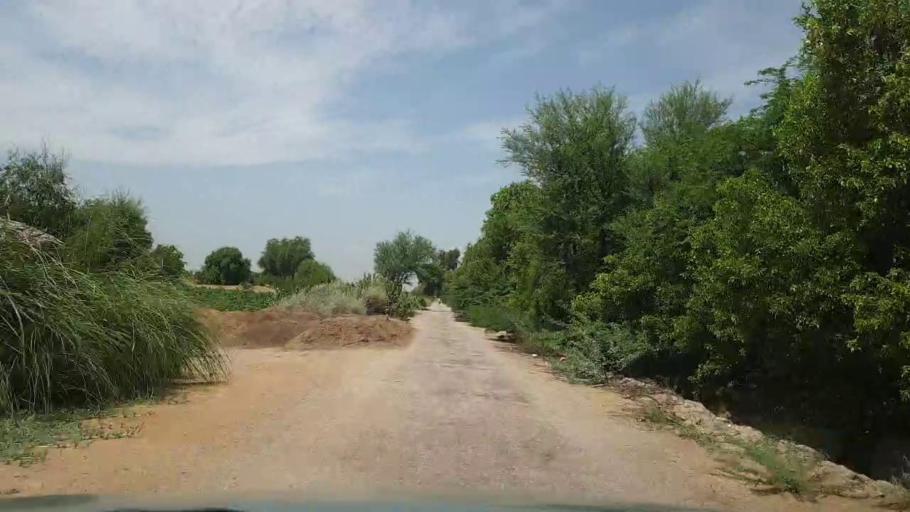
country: PK
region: Sindh
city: Bozdar
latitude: 27.0892
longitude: 69.0133
